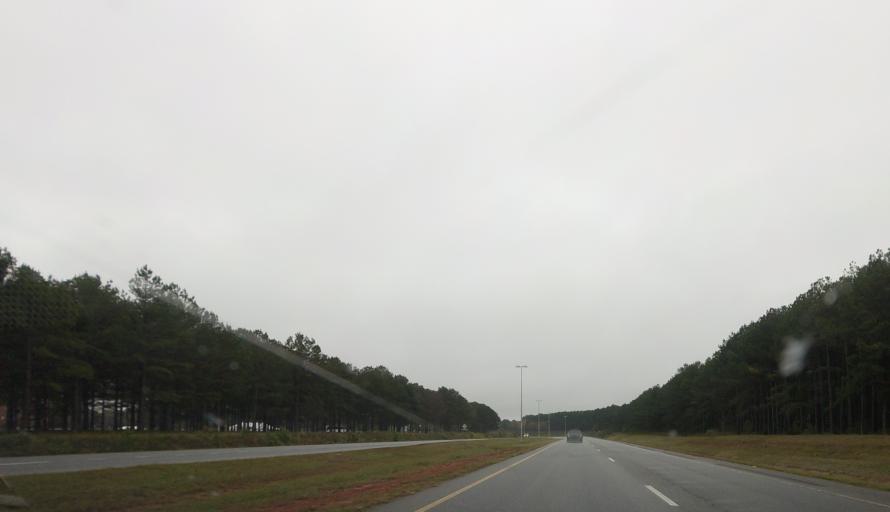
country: US
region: Georgia
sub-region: Houston County
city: Centerville
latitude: 32.5813
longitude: -83.6928
